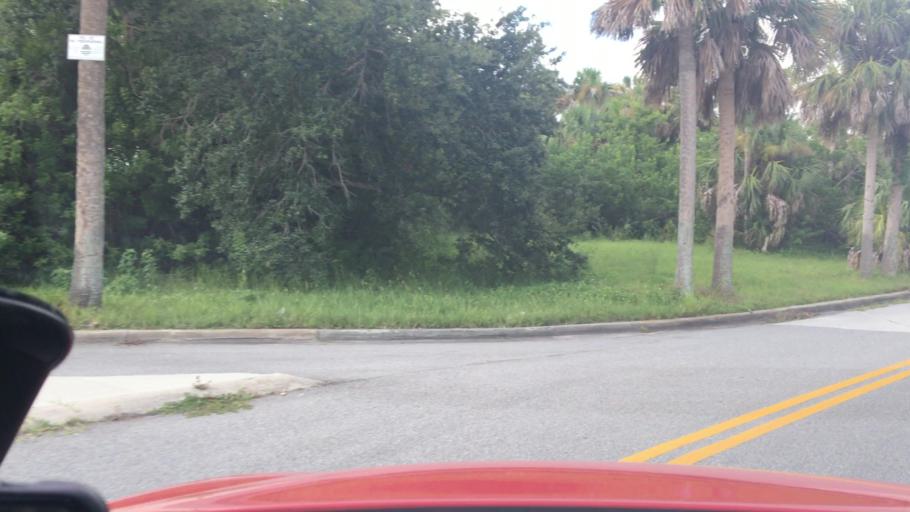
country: US
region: Florida
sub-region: Volusia County
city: South Daytona
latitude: 29.1648
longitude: -80.9970
